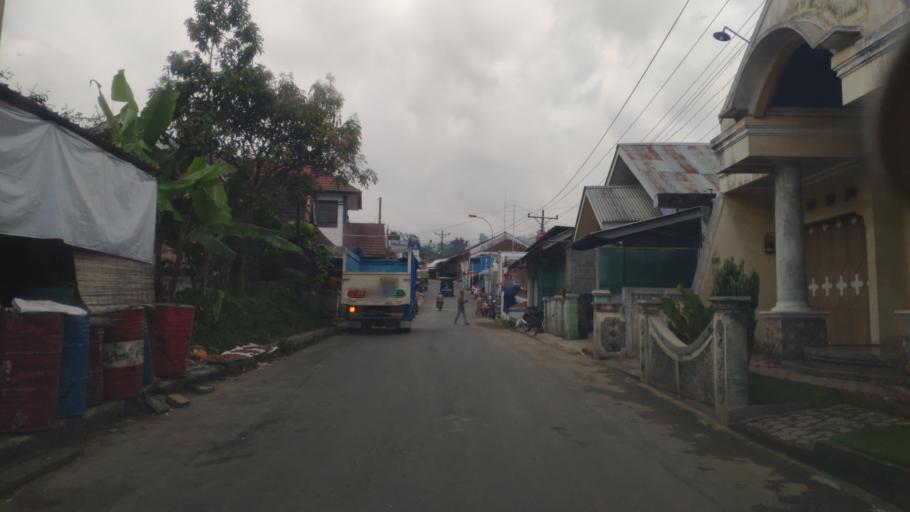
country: ID
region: Central Java
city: Wonosobo
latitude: -7.2489
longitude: 109.7944
